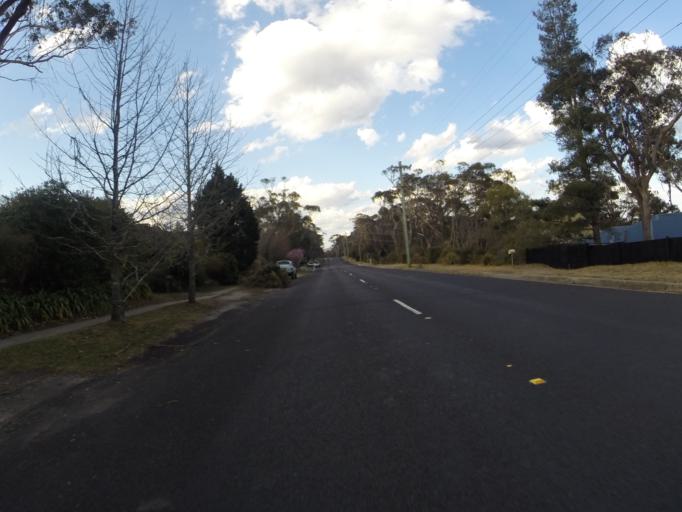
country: AU
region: New South Wales
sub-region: Blue Mountains Municipality
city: Blackheath
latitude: -33.6331
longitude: 150.3037
